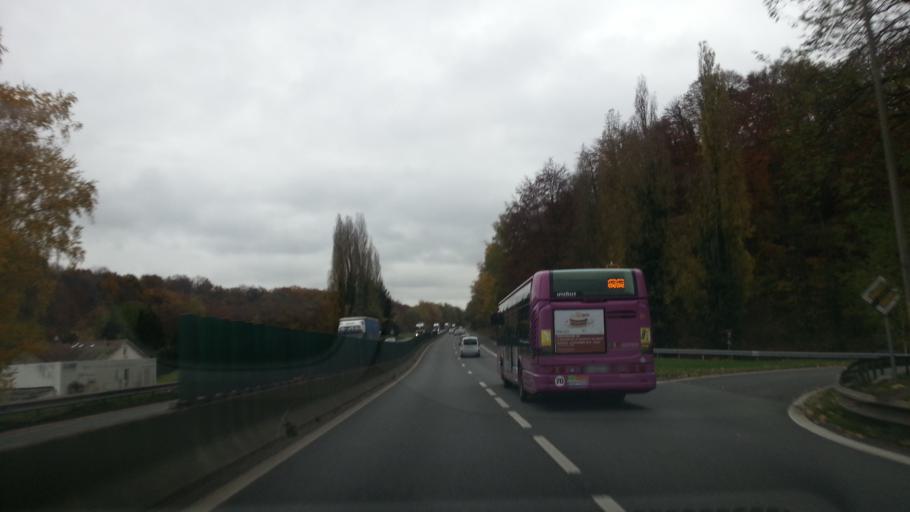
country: FR
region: Picardie
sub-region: Departement de l'Oise
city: Creil
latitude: 49.2641
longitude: 2.4869
